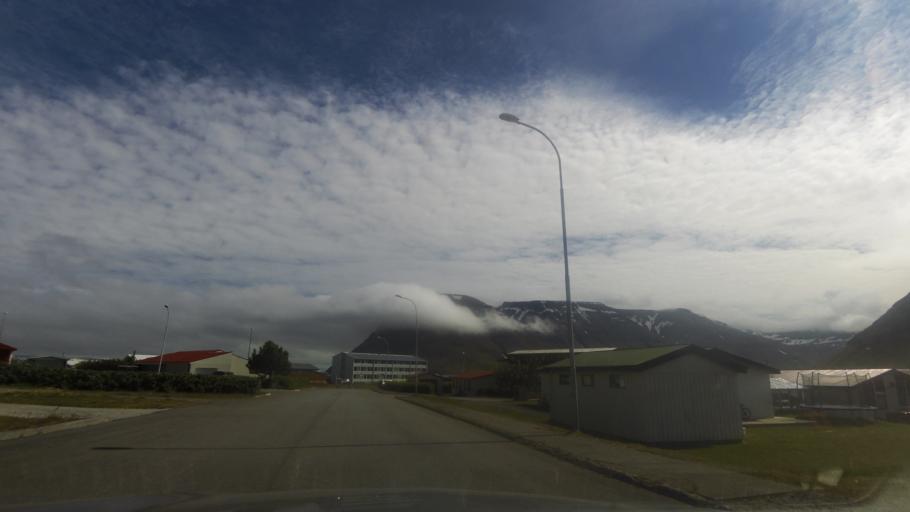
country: IS
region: Westfjords
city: Isafjoerdur
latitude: 66.1601
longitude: -23.2641
